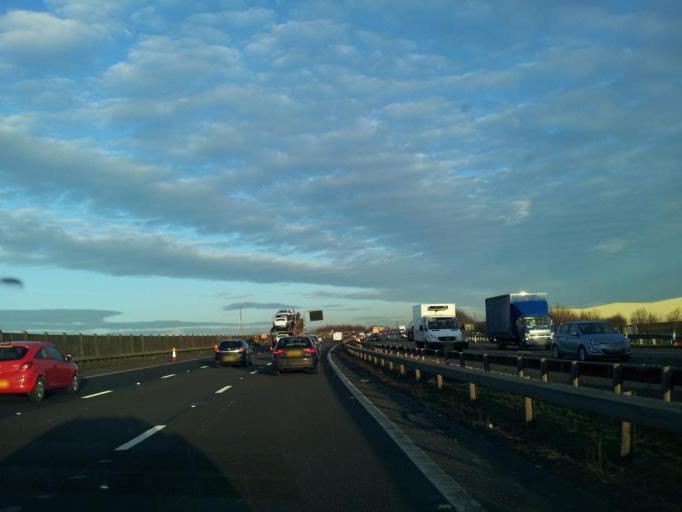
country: GB
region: England
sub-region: City and Borough of Wakefield
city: Normanton
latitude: 53.7115
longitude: -1.4152
